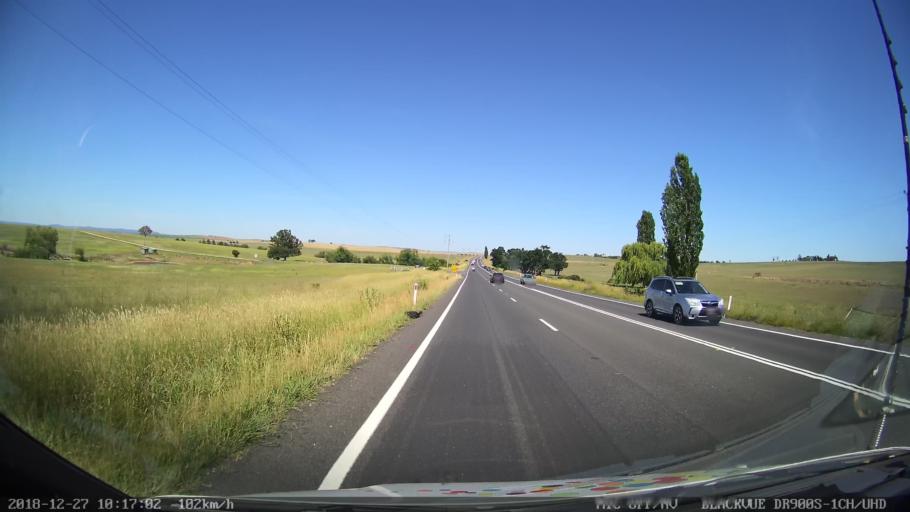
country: AU
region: New South Wales
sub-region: Bathurst Regional
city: Kelso
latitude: -33.4260
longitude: 149.6853
